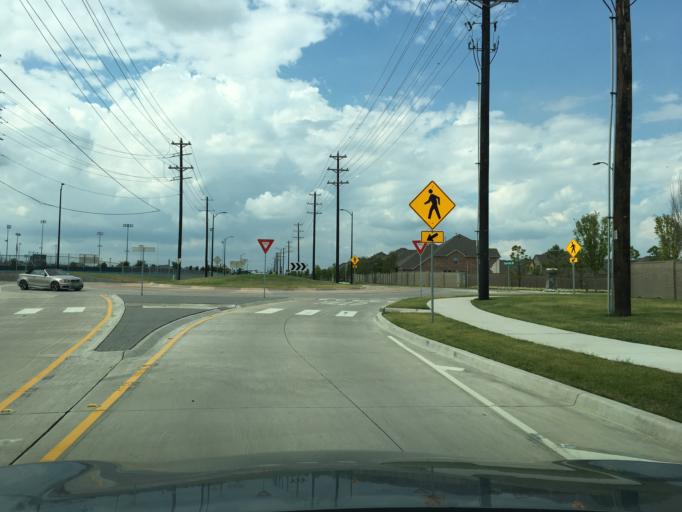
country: US
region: Texas
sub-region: Collin County
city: Frisco
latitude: 33.1289
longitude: -96.8604
